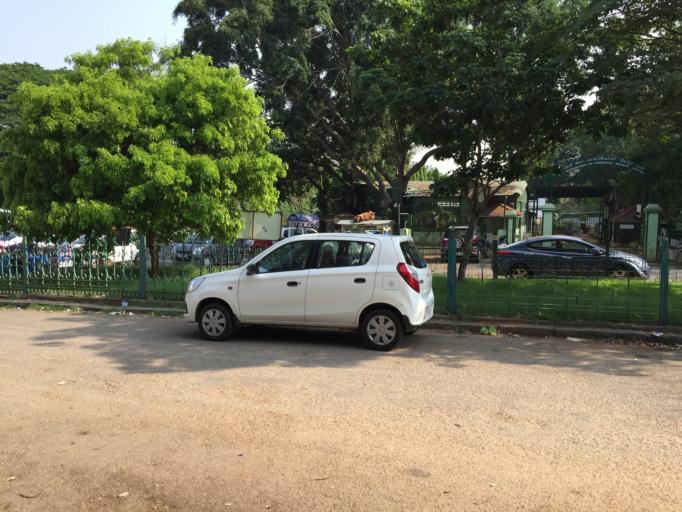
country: IN
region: Karnataka
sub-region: Bangalore Urban
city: Bangalore
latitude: 12.9495
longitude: 77.5902
